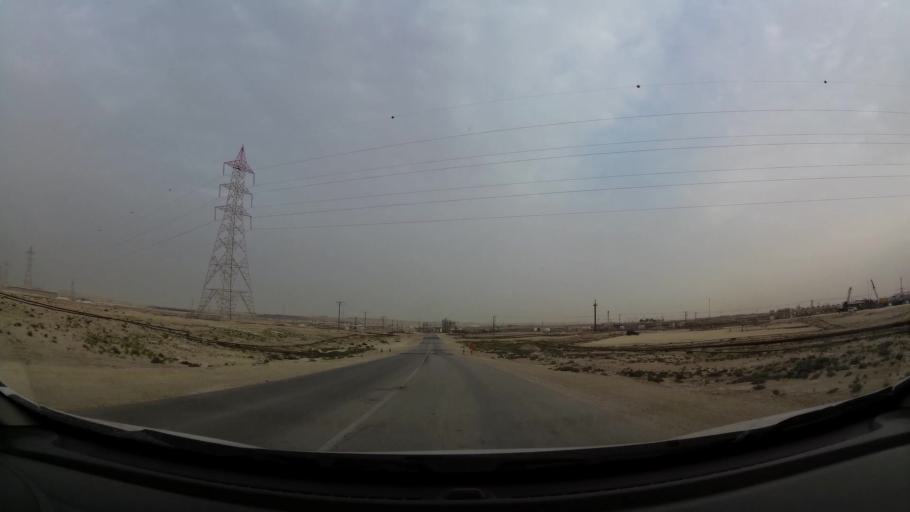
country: BH
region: Central Governorate
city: Dar Kulayb
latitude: 26.0200
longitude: 50.5724
